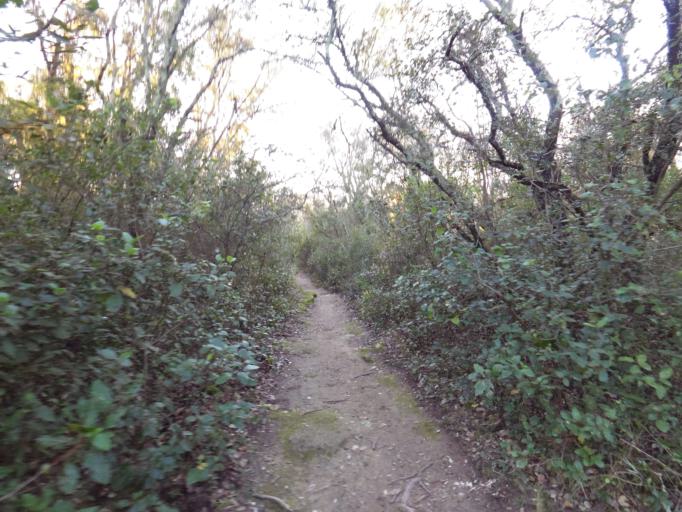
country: FR
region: Languedoc-Roussillon
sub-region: Departement du Gard
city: Villevieille
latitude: 43.7839
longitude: 4.1121
